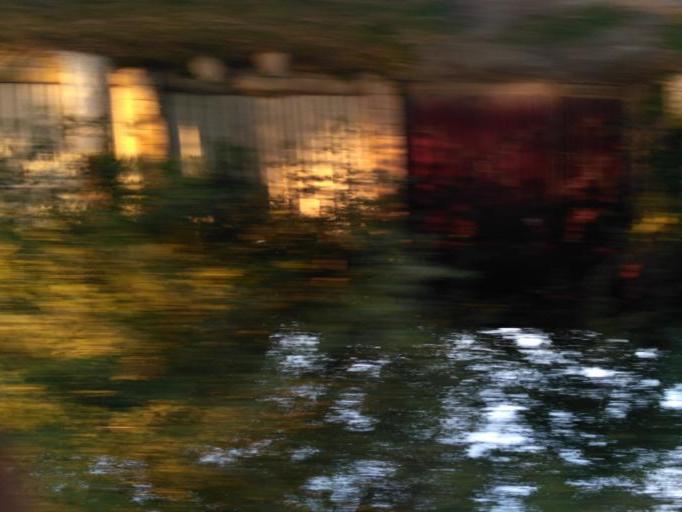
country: KZ
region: Almaty Qalasy
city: Almaty
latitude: 43.1779
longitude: 76.7481
